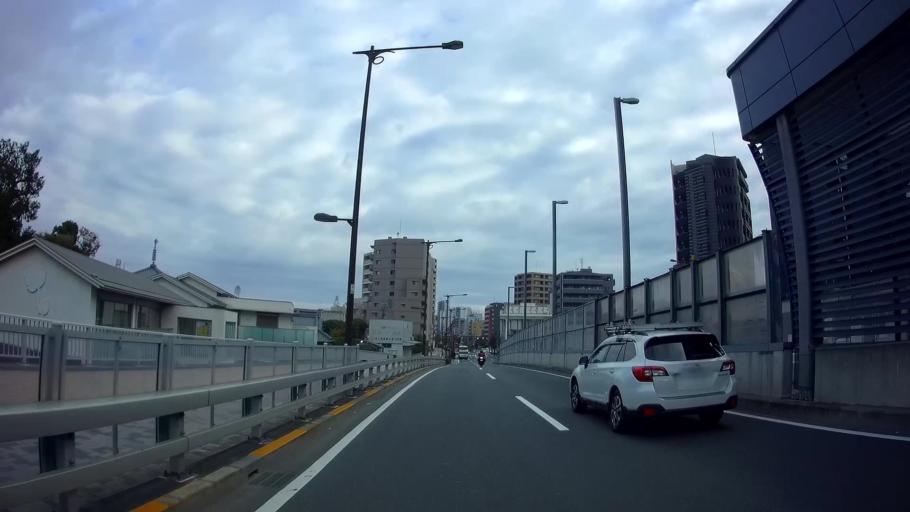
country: JP
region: Tokyo
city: Tokyo
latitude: 35.7265
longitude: 139.6956
